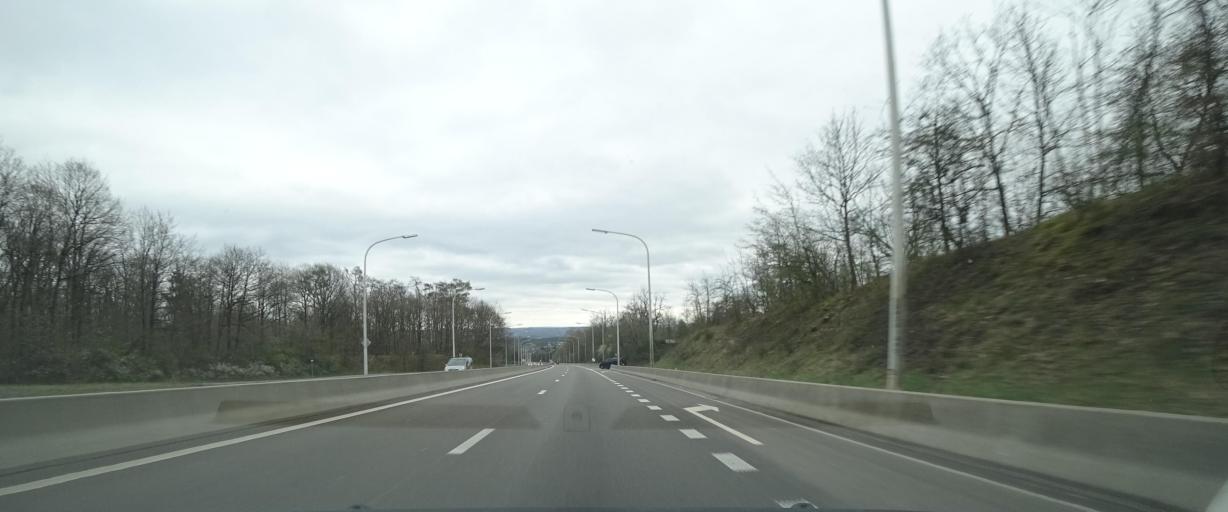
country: BE
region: Wallonia
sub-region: Province du Luxembourg
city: Marche-en-Famenne
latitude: 50.2571
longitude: 5.2667
